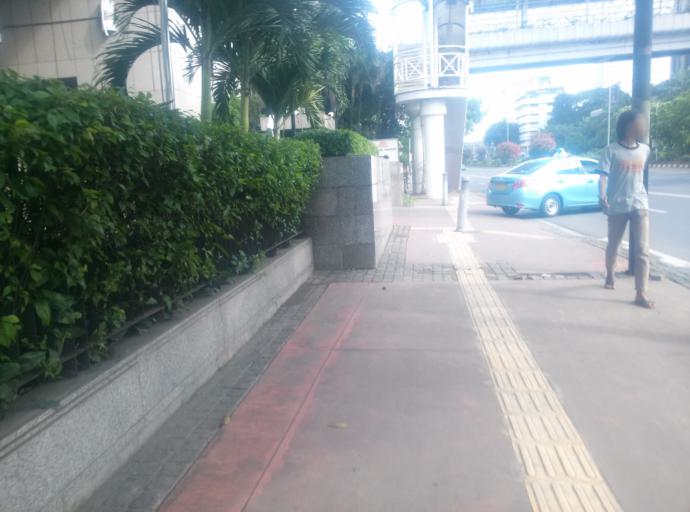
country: ID
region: Jakarta Raya
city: Jakarta
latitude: -6.1857
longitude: 106.8234
